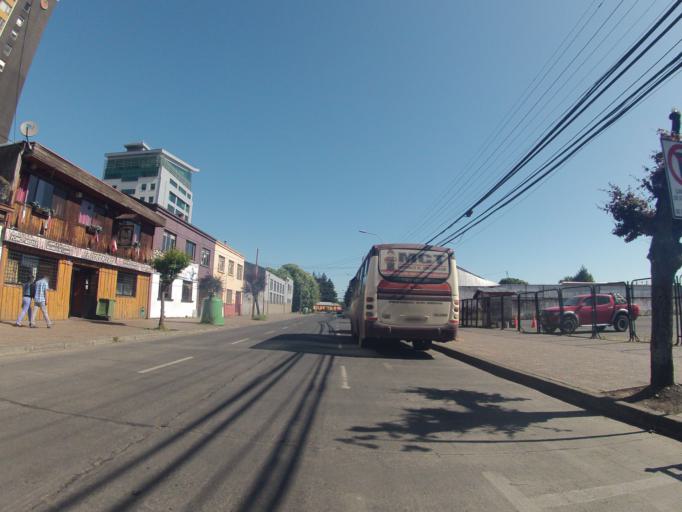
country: CL
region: Araucania
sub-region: Provincia de Cautin
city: Temuco
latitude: -38.7415
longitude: -72.5927
